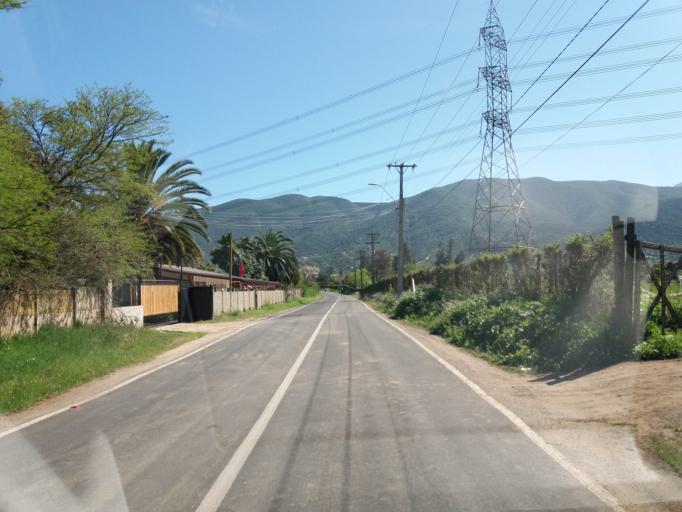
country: CL
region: Valparaiso
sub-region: Provincia de Marga Marga
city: Limache
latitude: -33.0043
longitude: -71.1916
